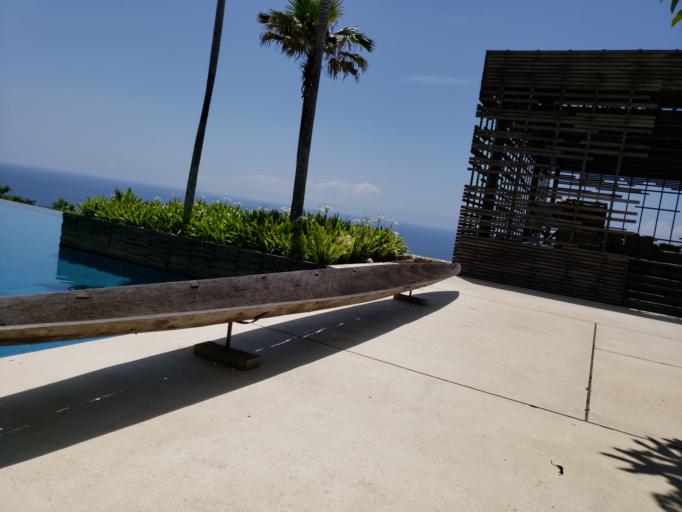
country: ID
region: Bali
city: Kangin
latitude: -8.8464
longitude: 115.1372
